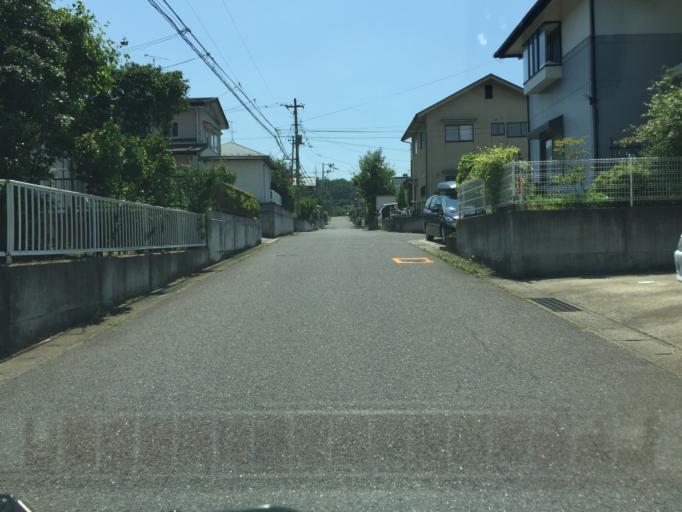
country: JP
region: Fukushima
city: Fukushima-shi
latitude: 37.7232
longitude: 140.4084
